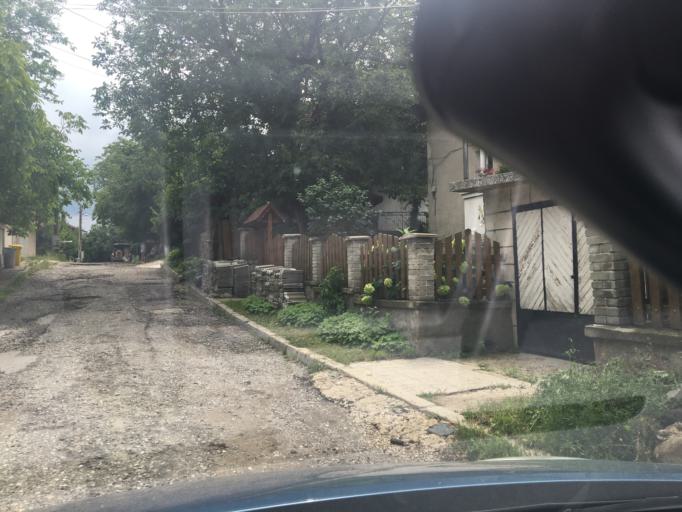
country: BG
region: Sofia-Capital
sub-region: Stolichna Obshtina
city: Sofia
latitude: 42.5839
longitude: 23.3676
